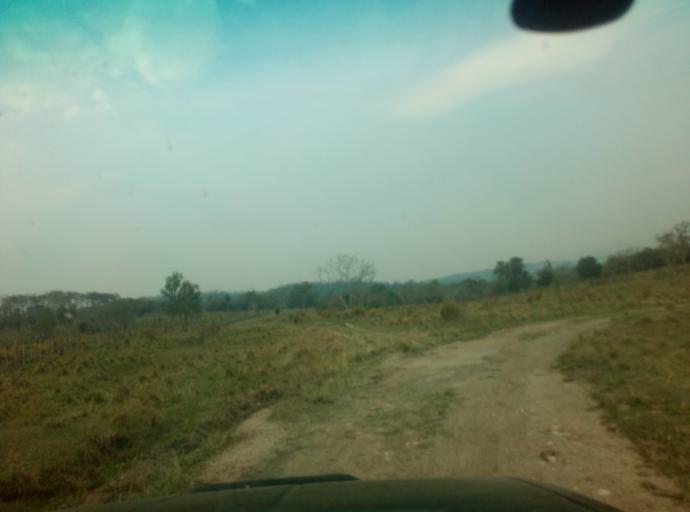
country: PY
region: Caaguazu
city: San Joaquin
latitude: -25.1018
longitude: -56.1239
